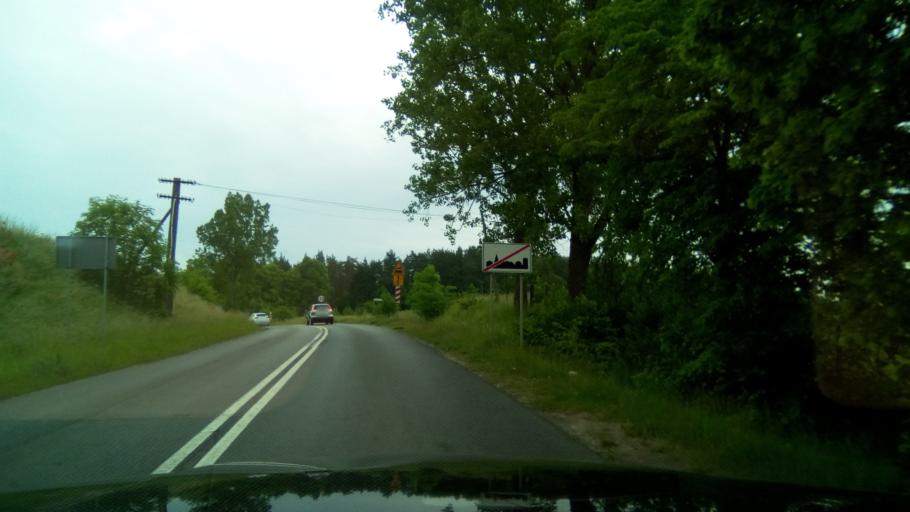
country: PL
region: Kujawsko-Pomorskie
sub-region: Powiat sepolenski
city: Wiecbork
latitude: 53.3671
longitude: 17.4954
